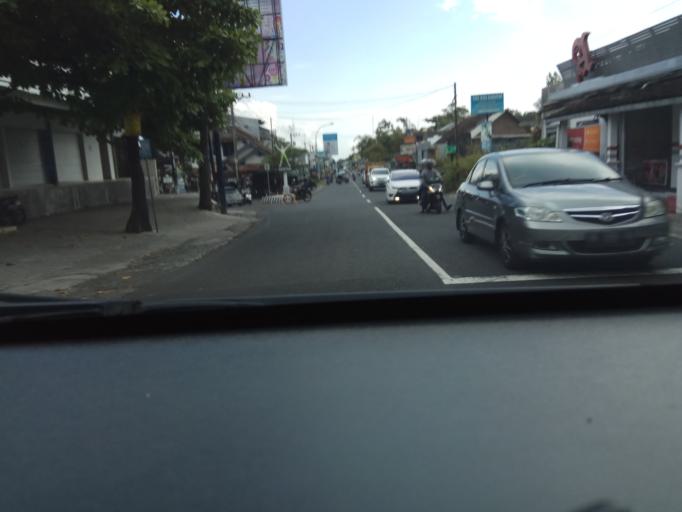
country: ID
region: Daerah Istimewa Yogyakarta
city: Melati
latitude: -7.7191
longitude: 110.4042
